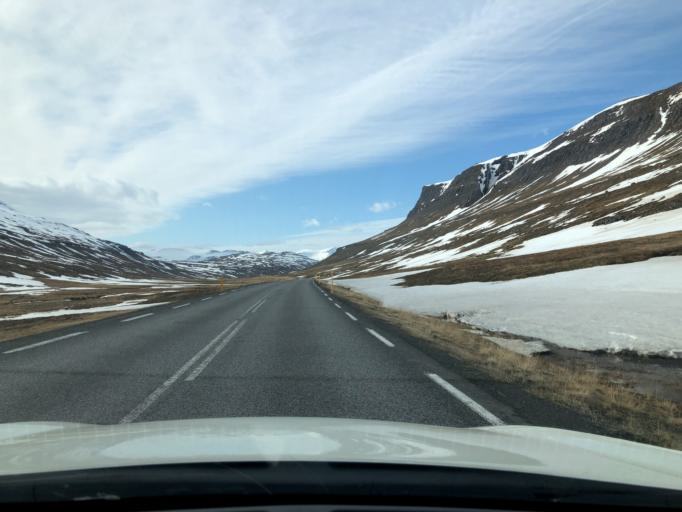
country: IS
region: East
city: Reydarfjoerdur
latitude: 65.1211
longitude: -14.3327
